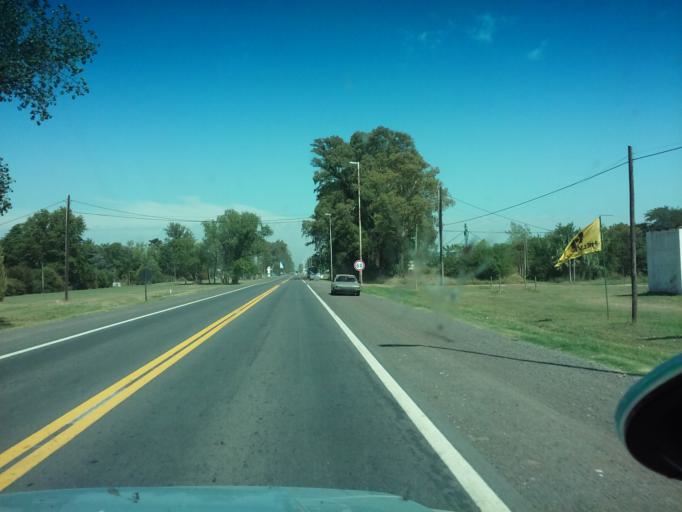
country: AR
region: Buenos Aires
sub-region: Partido de Nueve de Julio
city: Nueve de Julio
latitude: -35.4778
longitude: -60.8685
